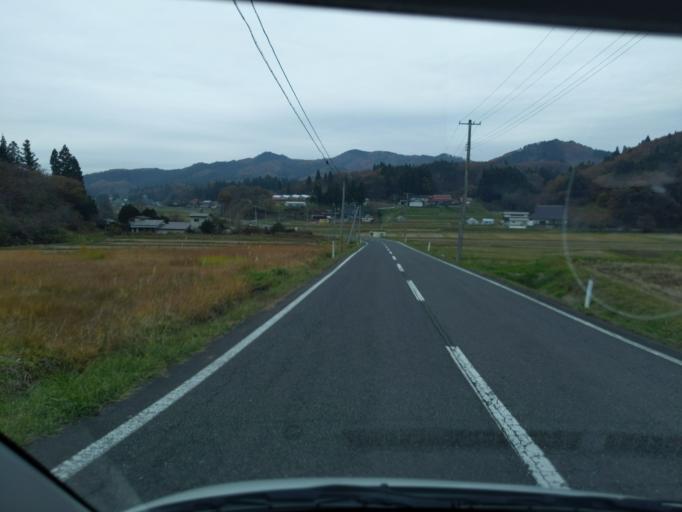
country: JP
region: Iwate
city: Kitakami
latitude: 39.2559
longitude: 141.2053
